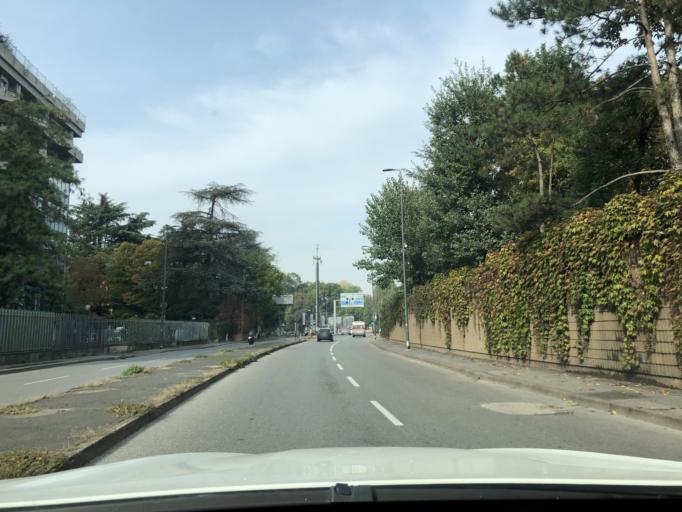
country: IT
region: Lombardy
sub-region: Citta metropolitana di Milano
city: Pero
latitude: 45.4827
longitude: 9.1186
